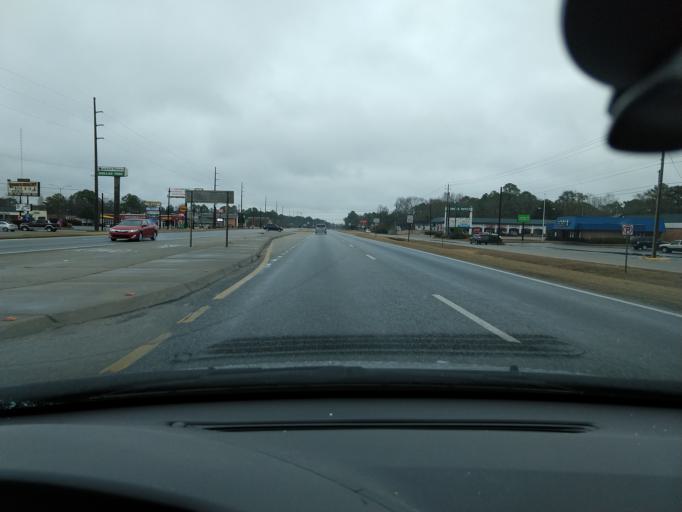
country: US
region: Alabama
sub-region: Houston County
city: Dothan
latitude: 31.2303
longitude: -85.4320
